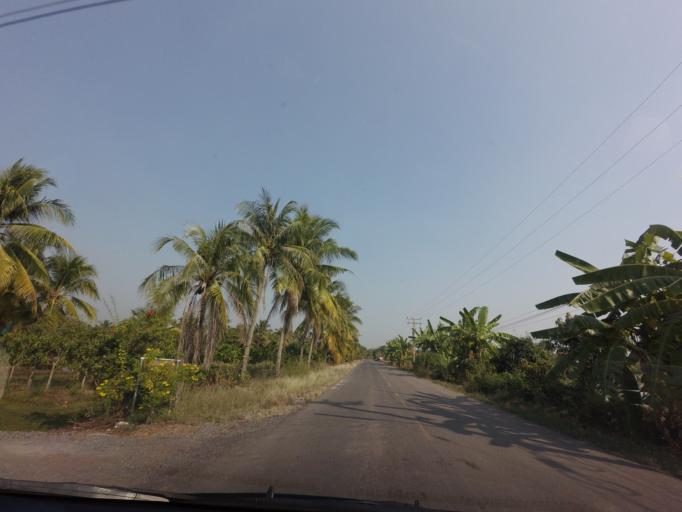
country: TH
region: Chachoengsao
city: Khlong Khuean
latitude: 13.7646
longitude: 101.1829
